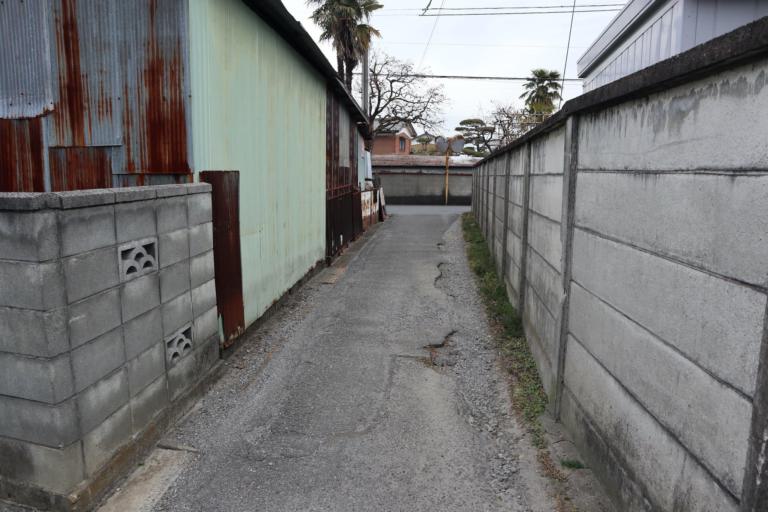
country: JP
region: Saitama
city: Fukiage-fujimi
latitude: 36.1089
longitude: 139.4494
